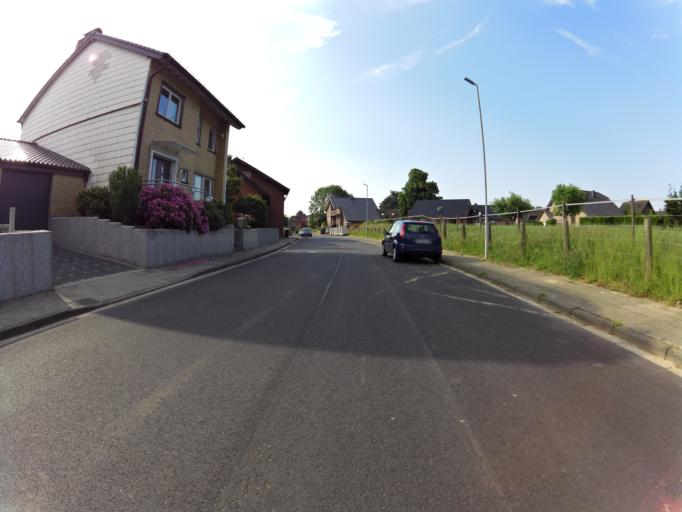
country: DE
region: North Rhine-Westphalia
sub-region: Regierungsbezirk Koln
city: Linnich
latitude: 50.9596
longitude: 6.2213
